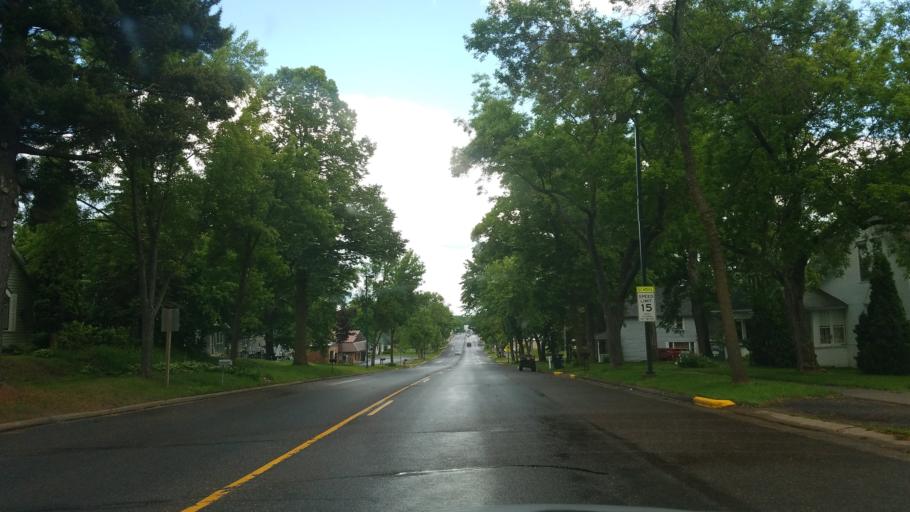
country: US
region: Wisconsin
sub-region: Polk County
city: Frederic
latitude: 45.6644
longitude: -92.4662
